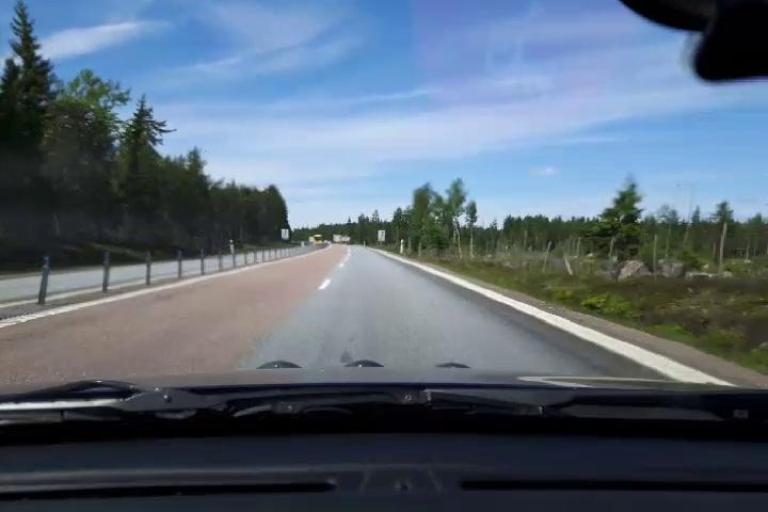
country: SE
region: Gaevleborg
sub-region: Gavle Kommun
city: Norrsundet
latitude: 60.8434
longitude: 17.0758
